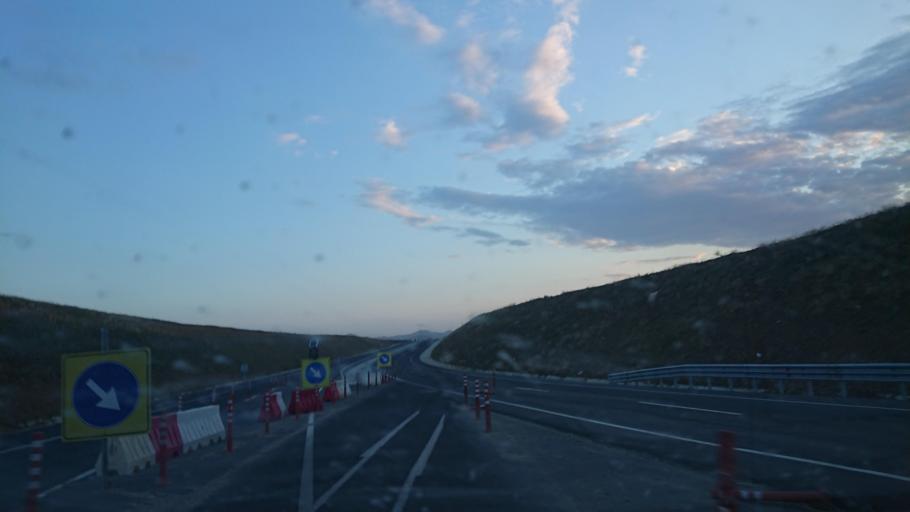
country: TR
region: Aksaray
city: Balci
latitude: 38.7820
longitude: 34.1171
